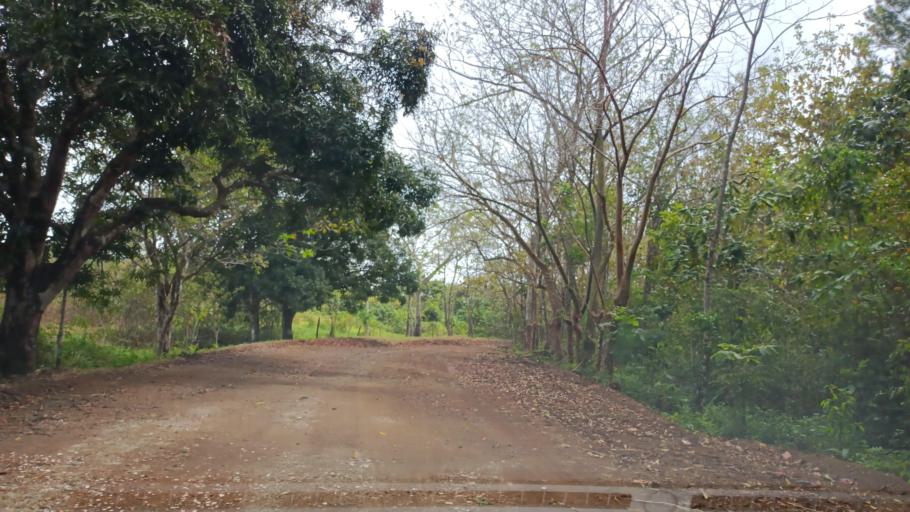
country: PA
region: Panama
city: La Cabima
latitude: 9.1323
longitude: -79.5140
